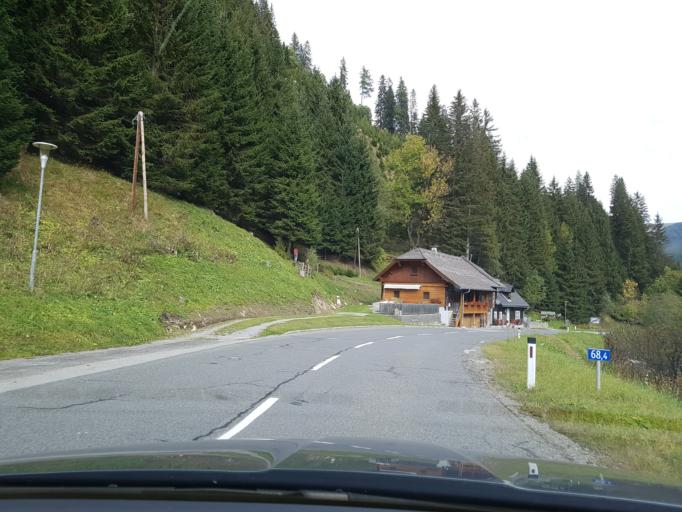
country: AT
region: Salzburg
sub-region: Politischer Bezirk Tamsweg
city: Ramingstein
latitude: 46.9651
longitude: 13.8867
